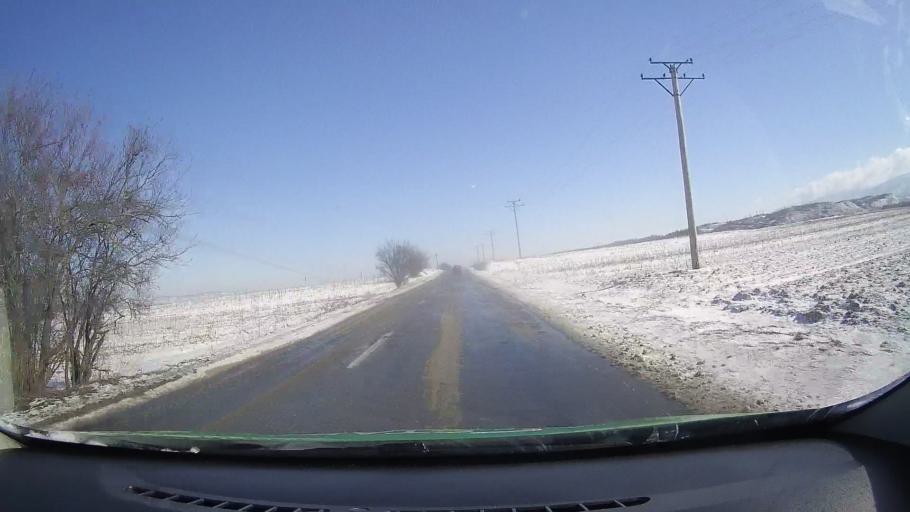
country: RO
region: Sibiu
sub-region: Comuna Racovita
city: Racovita
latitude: 45.6749
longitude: 24.3265
